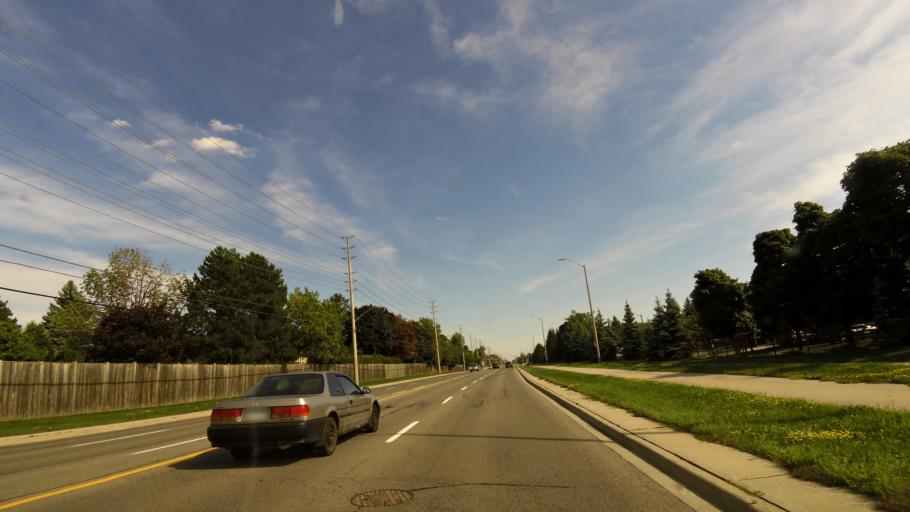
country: CA
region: Ontario
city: Mississauga
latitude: 43.5333
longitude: -79.6961
